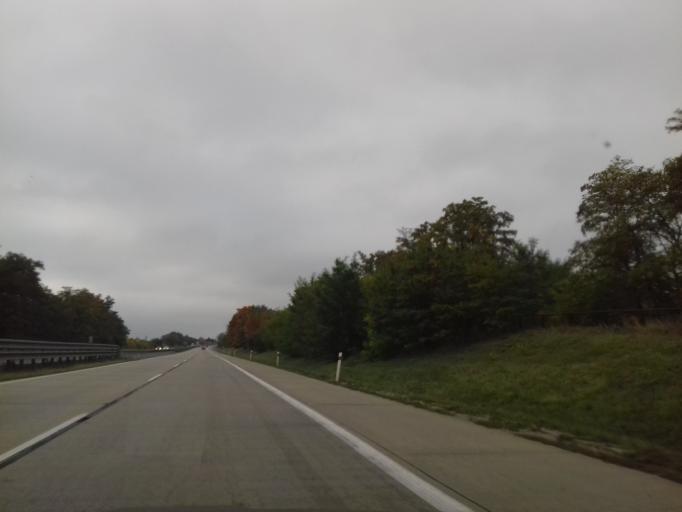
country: CZ
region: South Moravian
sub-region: Okres Breclav
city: Hustopece
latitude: 48.9305
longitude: 16.7536
